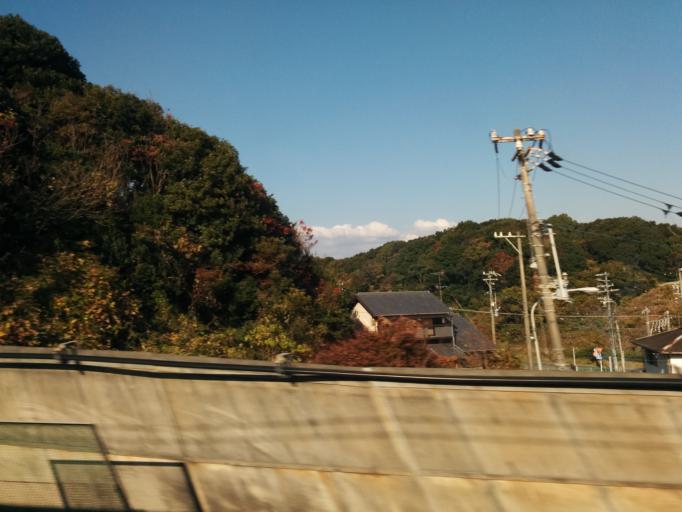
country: JP
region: Shizuoka
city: Kosai-shi
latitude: 34.6973
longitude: 137.5571
